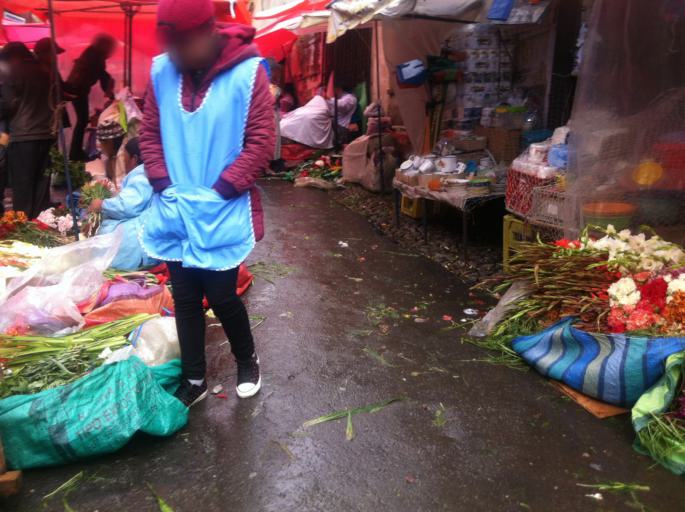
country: BO
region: La Paz
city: La Paz
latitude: -16.4999
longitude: -68.1375
